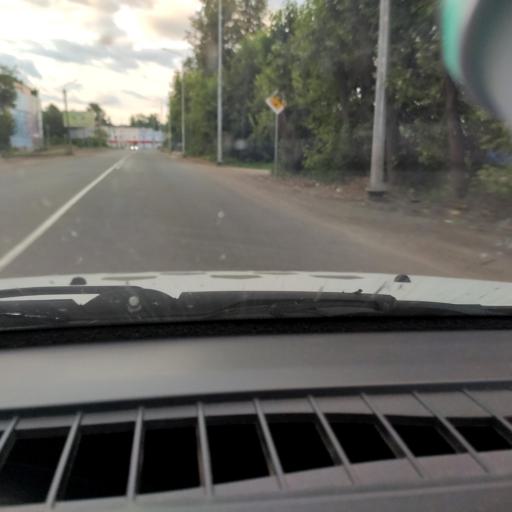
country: RU
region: Kirov
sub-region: Kirovo-Chepetskiy Rayon
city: Kirov
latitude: 58.6138
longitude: 49.7429
